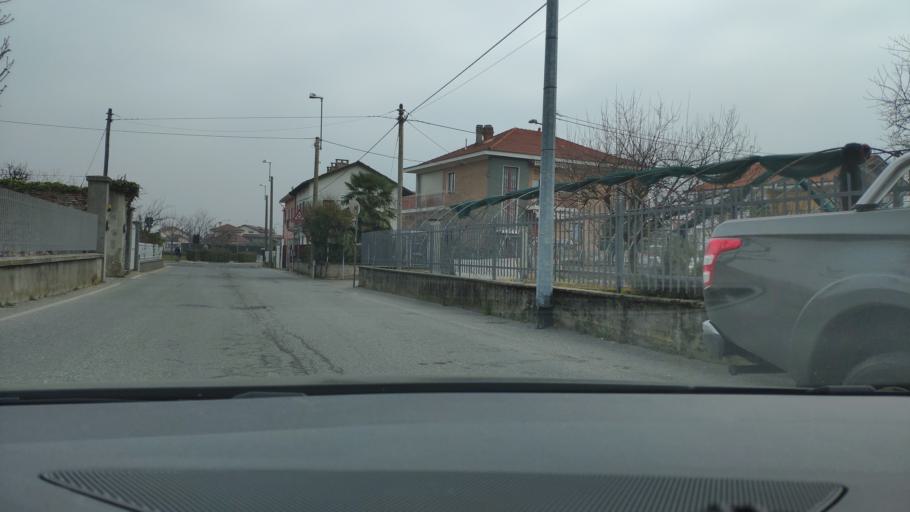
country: IT
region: Piedmont
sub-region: Provincia di Torino
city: Pianezza
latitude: 45.1137
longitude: 7.5426
